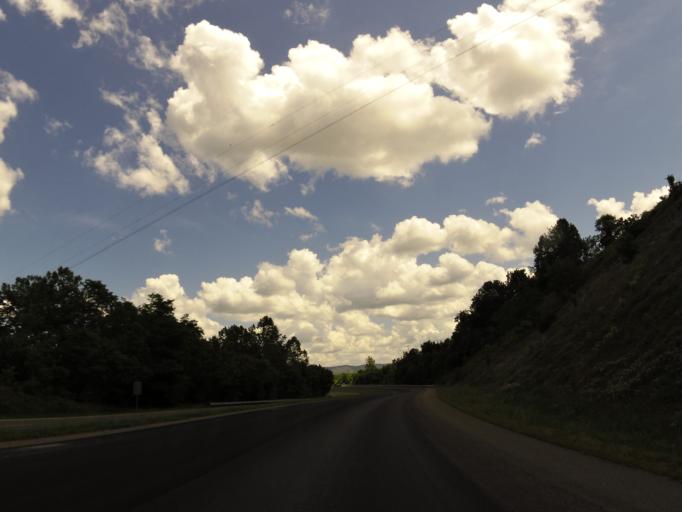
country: US
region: Virginia
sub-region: Lee County
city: Jonesville
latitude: 36.6733
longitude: -83.2054
